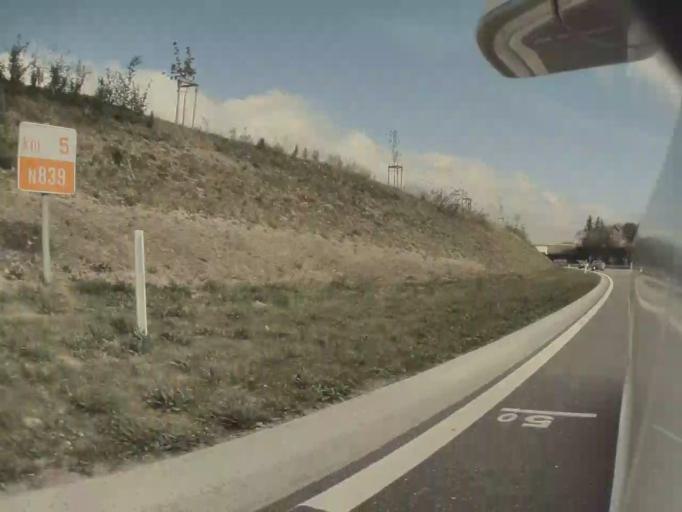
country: BE
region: Wallonia
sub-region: Province du Luxembourg
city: Marche-en-Famenne
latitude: 50.2250
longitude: 5.3149
